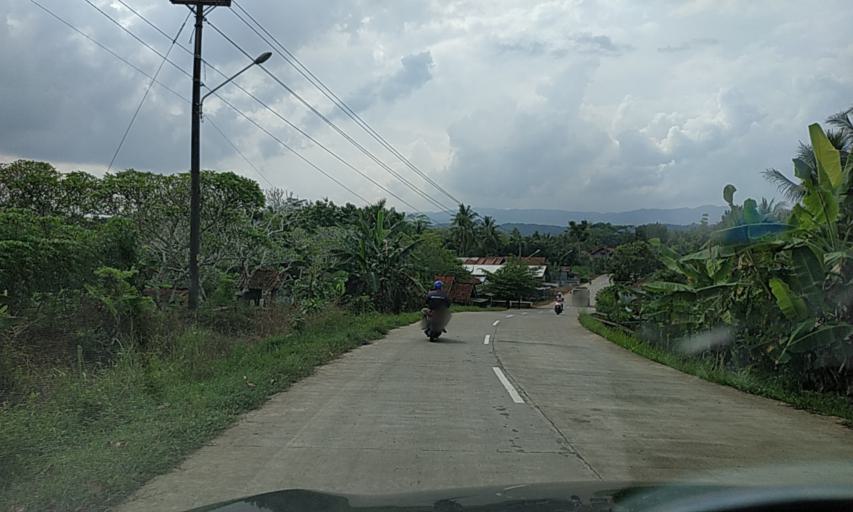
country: ID
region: Central Java
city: Winangun
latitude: -7.3623
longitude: 108.7008
